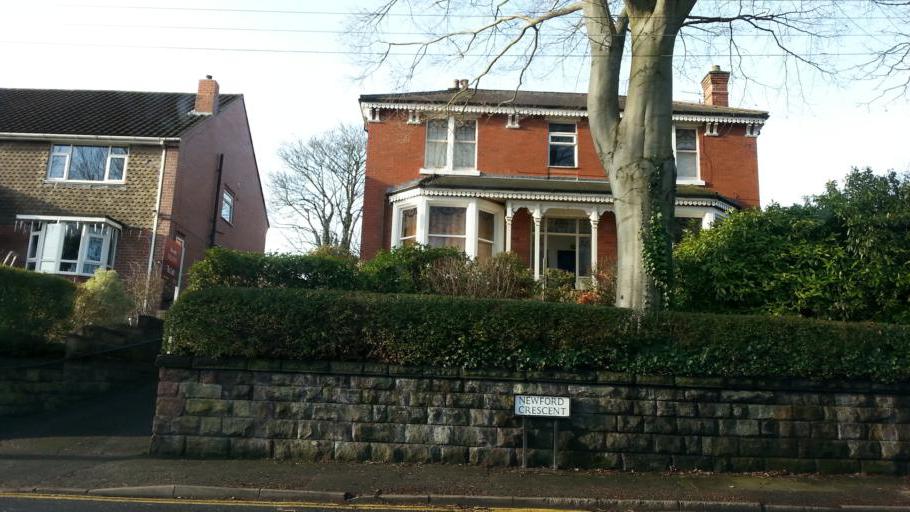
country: GB
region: England
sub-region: Stoke-on-Trent
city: Stoke-on-Trent
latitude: 53.0503
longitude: -2.1514
